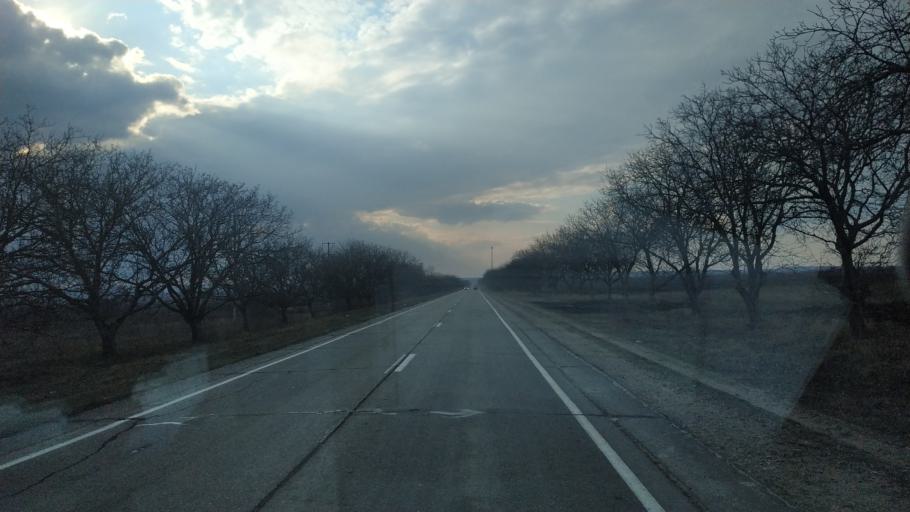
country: MD
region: Anenii Noi
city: Varnita
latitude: 46.9223
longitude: 29.3914
